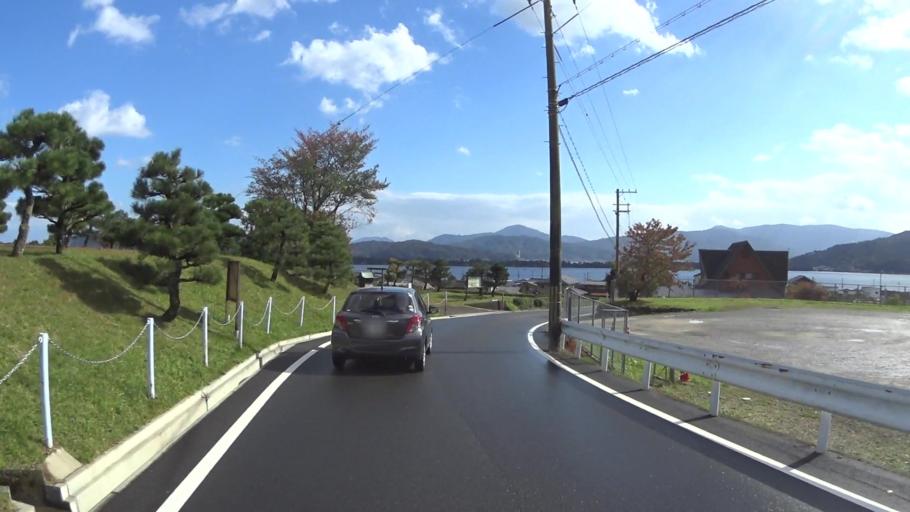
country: JP
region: Kyoto
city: Miyazu
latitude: 35.5796
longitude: 135.1783
